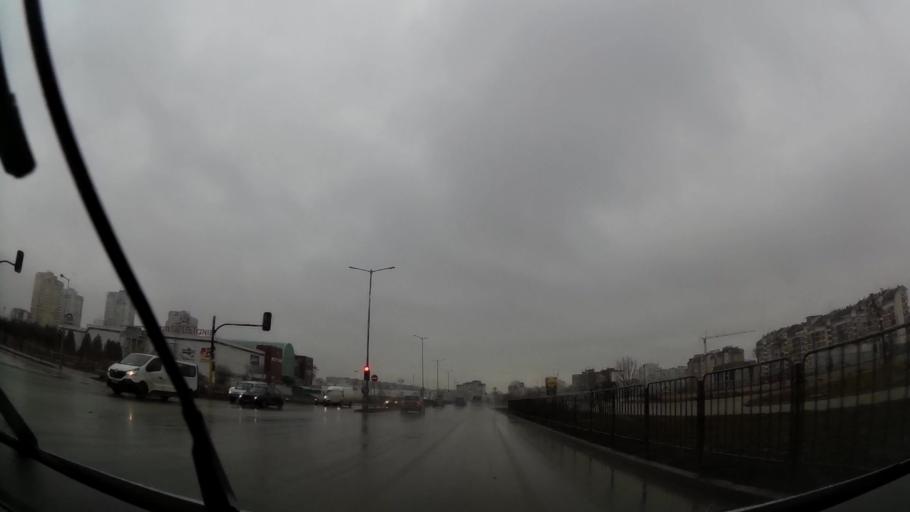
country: BG
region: Sofia-Capital
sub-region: Stolichna Obshtina
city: Sofia
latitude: 42.6352
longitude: 23.3732
